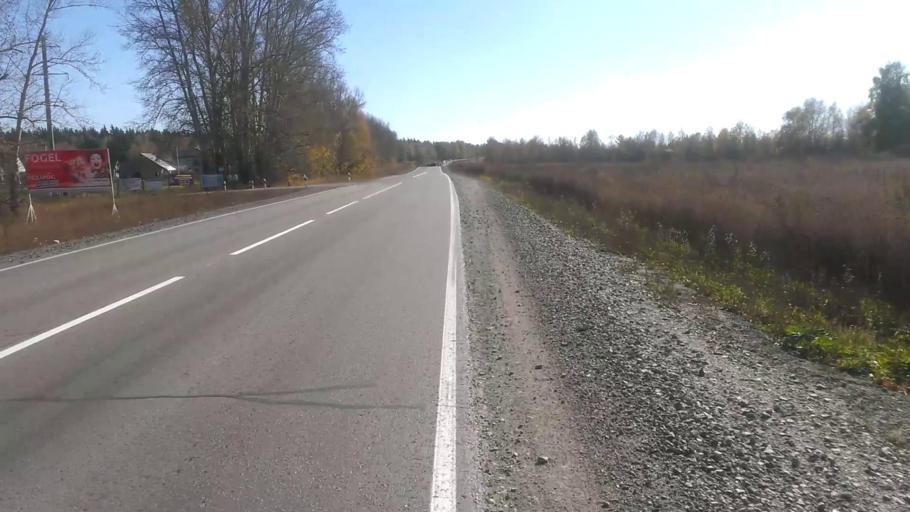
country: RU
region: Altai Krai
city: Sannikovo
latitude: 53.3076
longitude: 83.9679
